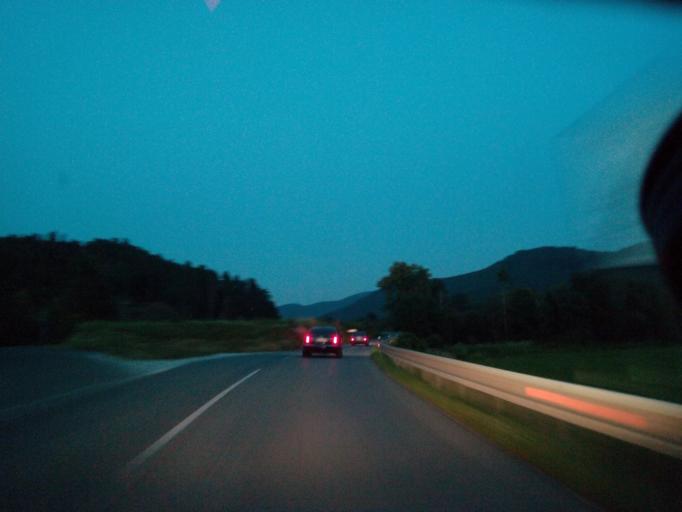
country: SK
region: Kosicky
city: Krompachy
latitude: 48.9412
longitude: 20.8214
